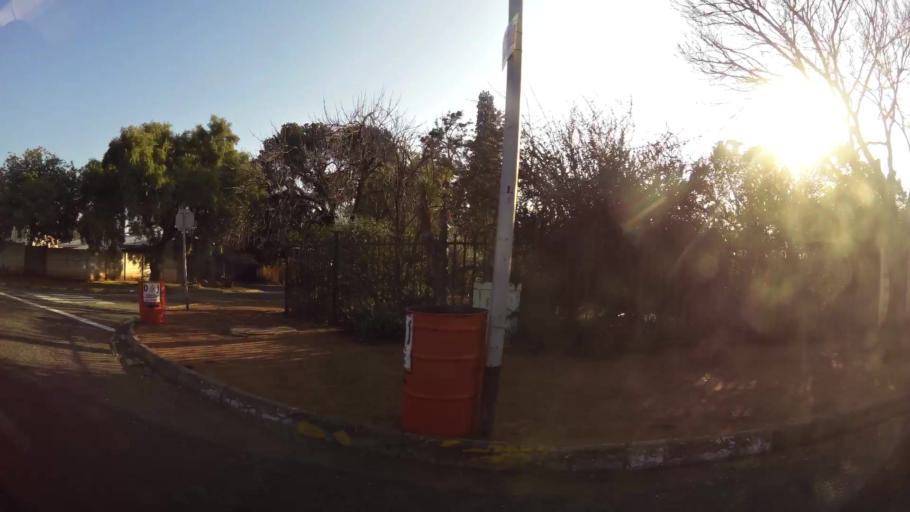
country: ZA
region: Orange Free State
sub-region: Mangaung Metropolitan Municipality
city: Bloemfontein
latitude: -29.1421
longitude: 26.2020
